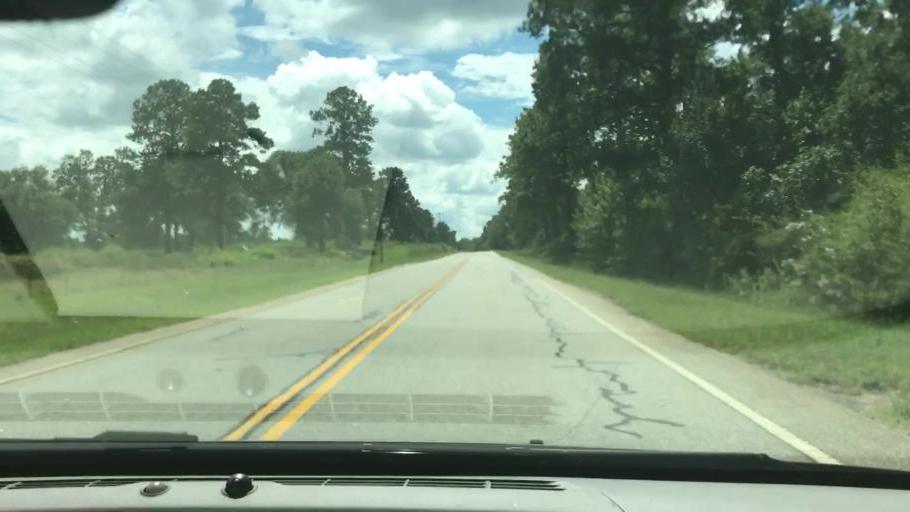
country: US
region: Georgia
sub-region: Quitman County
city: Georgetown
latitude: 32.1201
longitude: -85.0362
